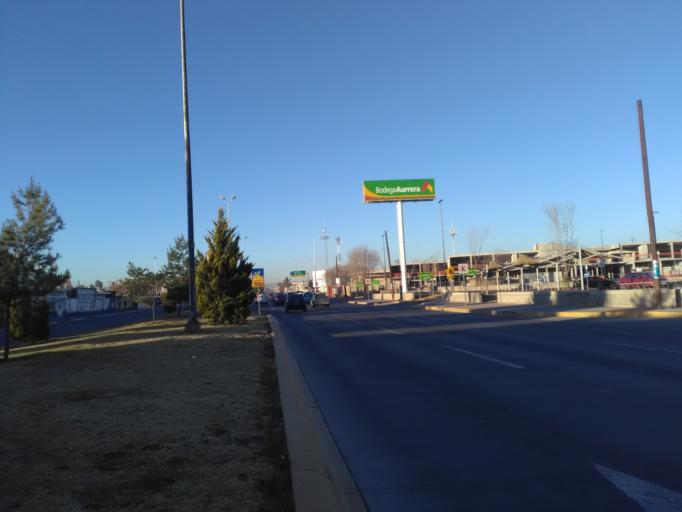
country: MX
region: Durango
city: Victoria de Durango
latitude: 24.0544
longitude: -104.6424
